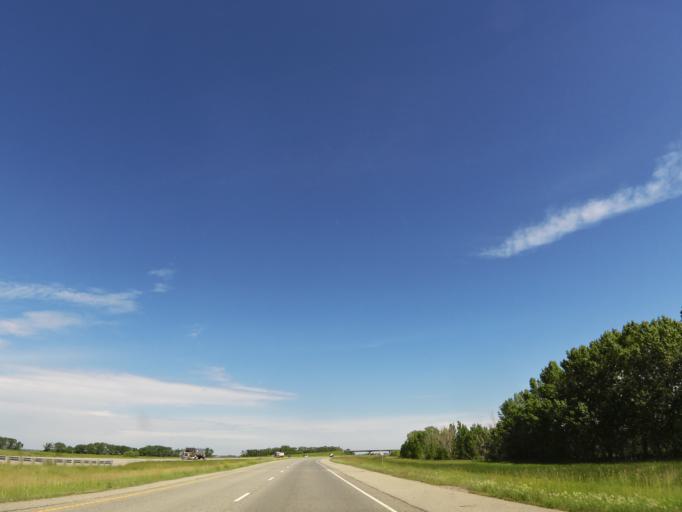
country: US
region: North Dakota
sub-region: Cass County
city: West Fargo
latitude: 47.0001
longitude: -96.8985
